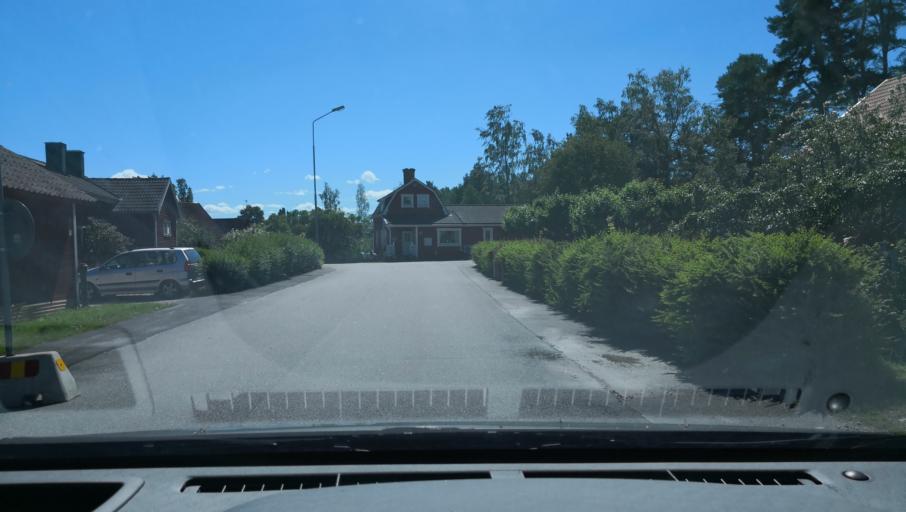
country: SE
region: Vaestmanland
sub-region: Kungsors Kommun
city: Kungsoer
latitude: 59.2796
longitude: 16.1124
